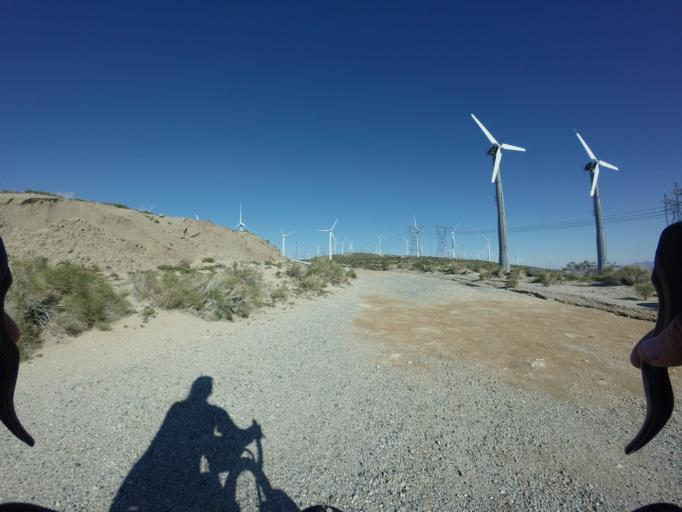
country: US
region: California
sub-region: Riverside County
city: Garnet
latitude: 33.9227
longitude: -116.6301
